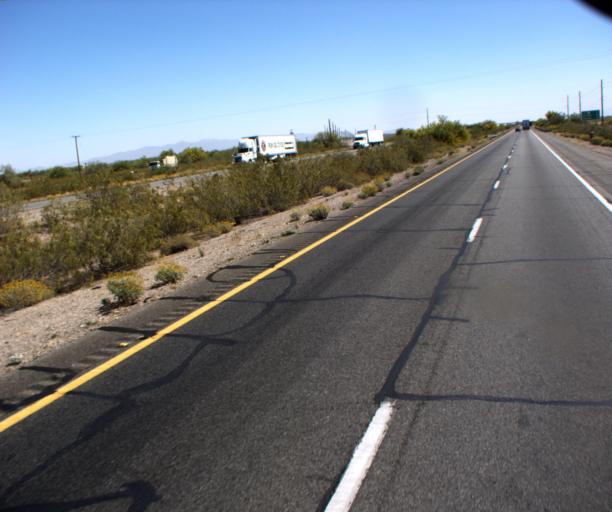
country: US
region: Arizona
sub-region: Maricopa County
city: Buckeye
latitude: 33.4936
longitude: -112.9209
